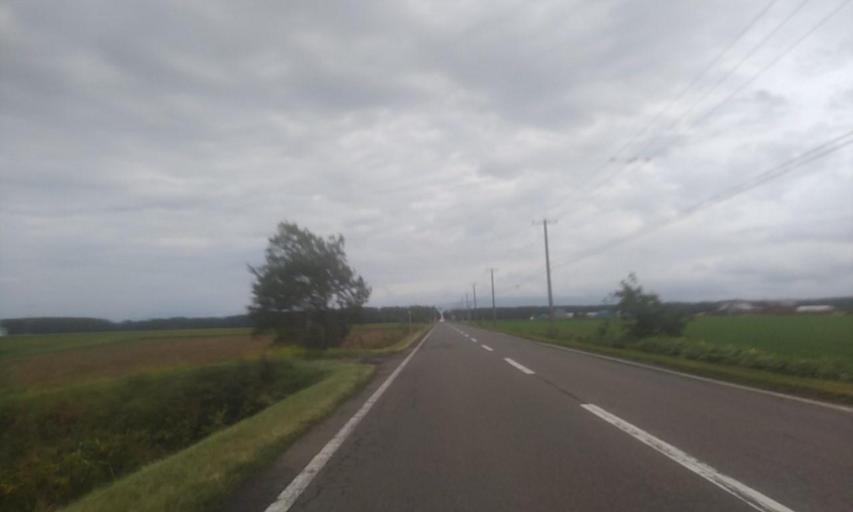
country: JP
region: Hokkaido
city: Abashiri
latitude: 43.8934
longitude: 144.5170
